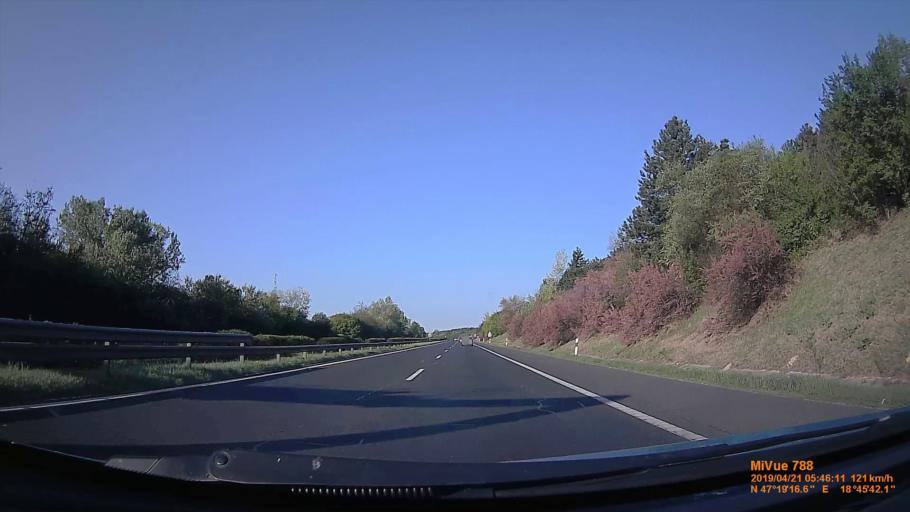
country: HU
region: Fejer
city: Martonvasar
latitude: 47.3210
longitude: 18.7608
